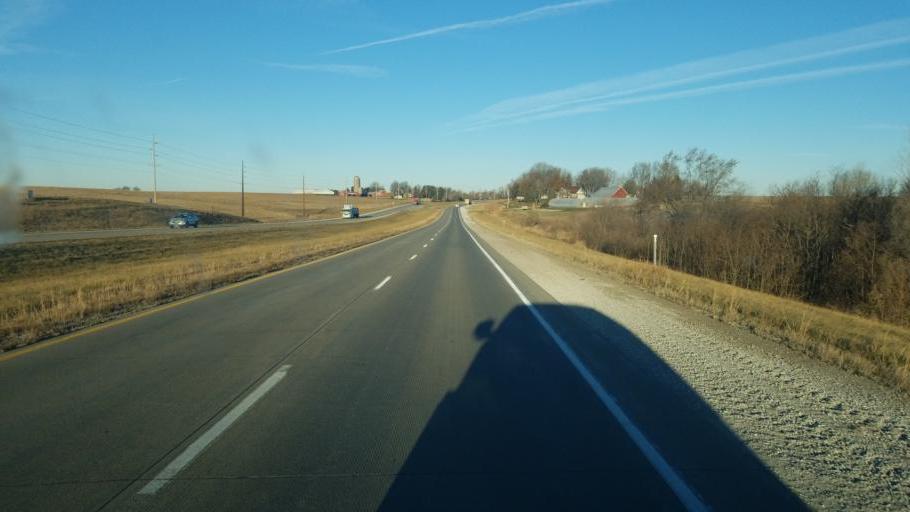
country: US
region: Iowa
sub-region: Mahaska County
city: Oskaloosa
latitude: 41.3464
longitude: -92.7492
